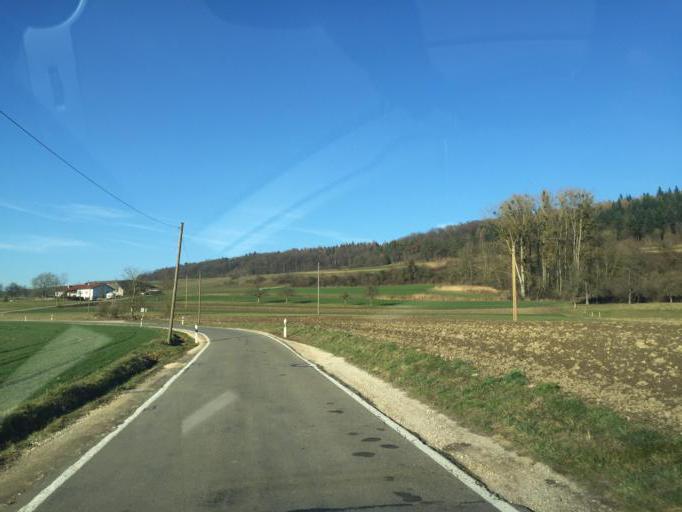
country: CH
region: Thurgau
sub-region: Frauenfeld District
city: Diessenhofen
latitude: 47.6999
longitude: 8.7347
